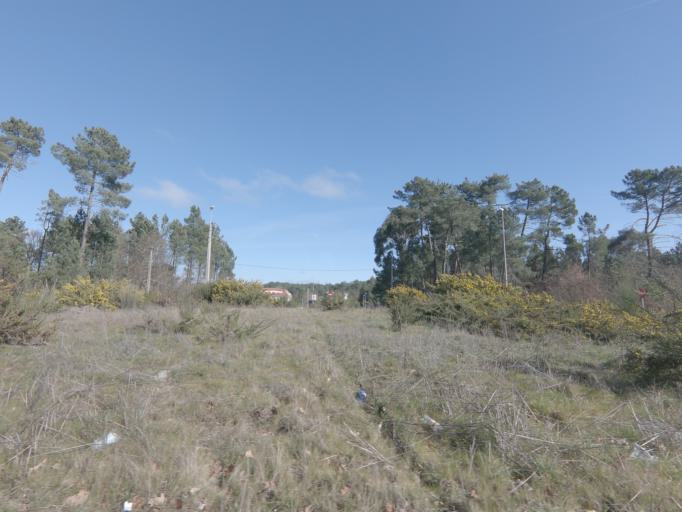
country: ES
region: Galicia
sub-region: Provincia de Ourense
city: Maside
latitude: 42.4529
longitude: -8.0282
